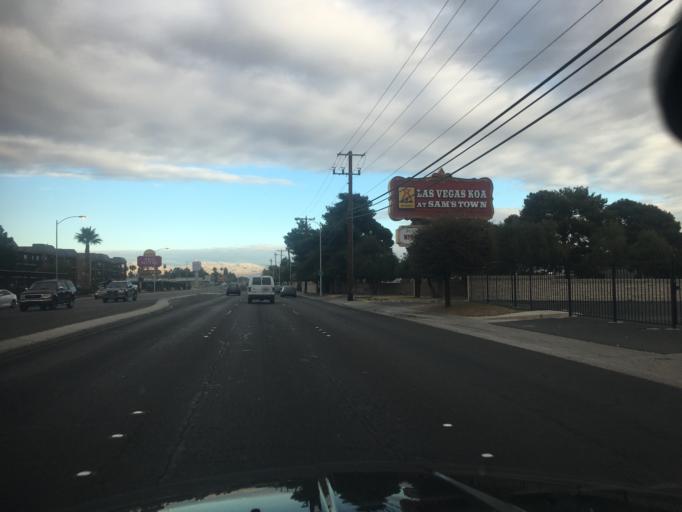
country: US
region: Nevada
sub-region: Clark County
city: Whitney
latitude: 36.1156
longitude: -115.0647
